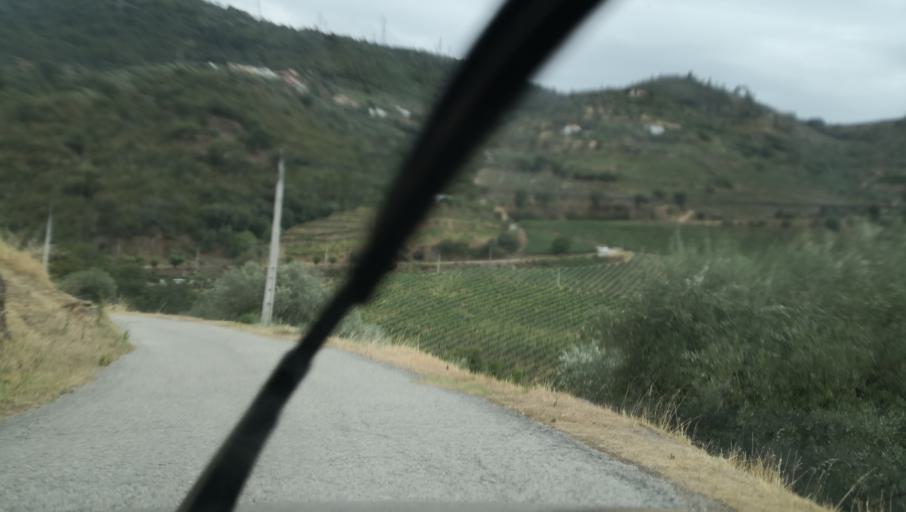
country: PT
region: Viseu
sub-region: Armamar
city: Armamar
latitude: 41.1308
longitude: -7.6322
